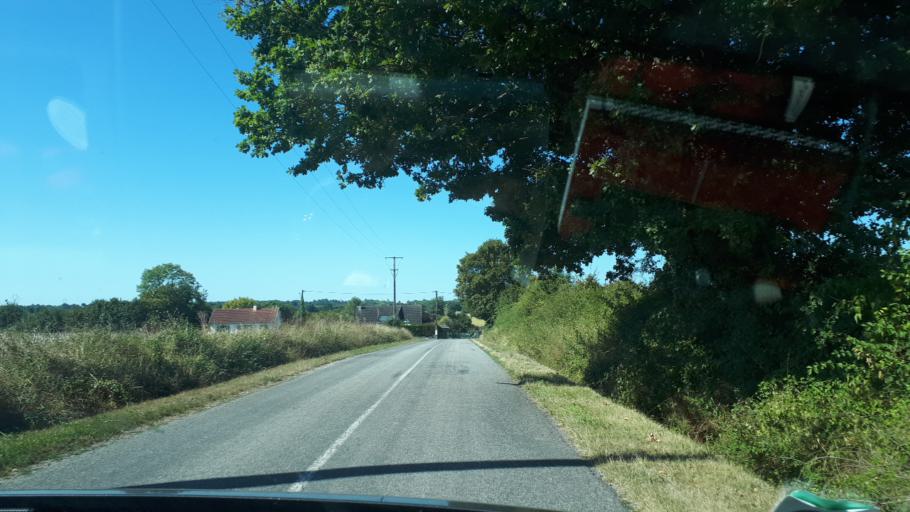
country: FR
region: Centre
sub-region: Departement du Loiret
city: Autry-le-Chatel
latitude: 47.5931
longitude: 2.6095
